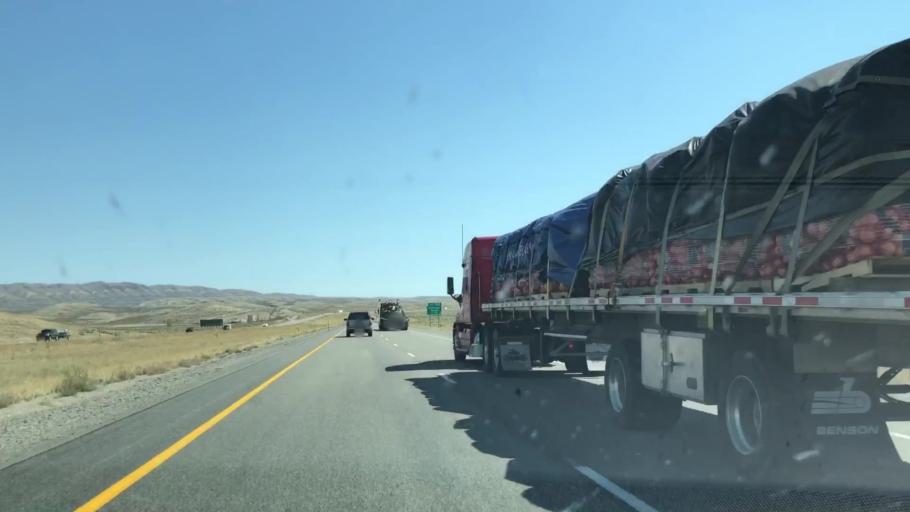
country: US
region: Wyoming
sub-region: Carbon County
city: Saratoga
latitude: 41.7417
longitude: -106.7847
